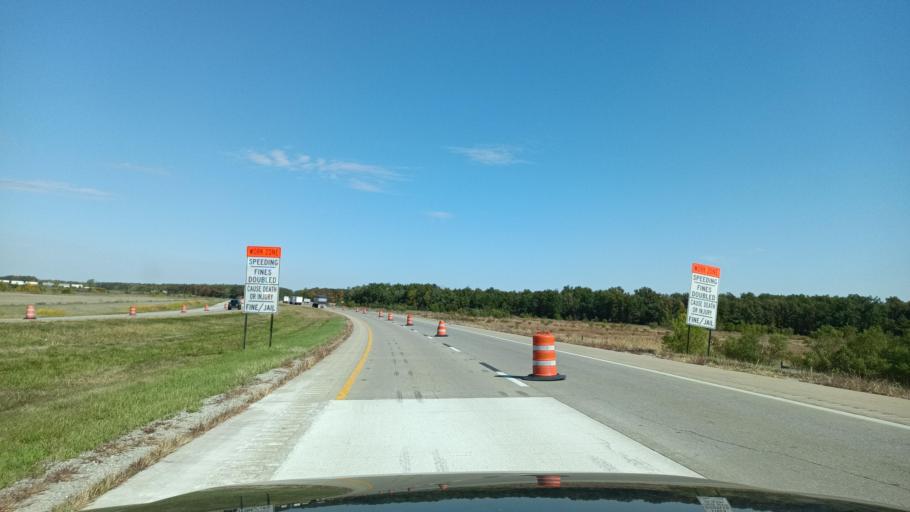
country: US
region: Ohio
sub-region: Defiance County
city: Defiance
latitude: 41.2628
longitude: -84.4347
